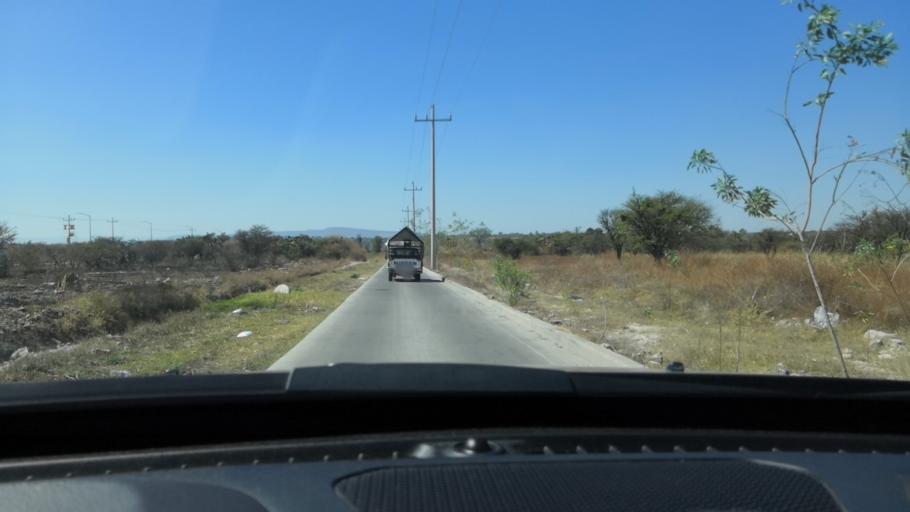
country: MX
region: Guanajuato
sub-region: Leon
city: Centro Familiar la Soledad
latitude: 21.1061
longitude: -101.7664
